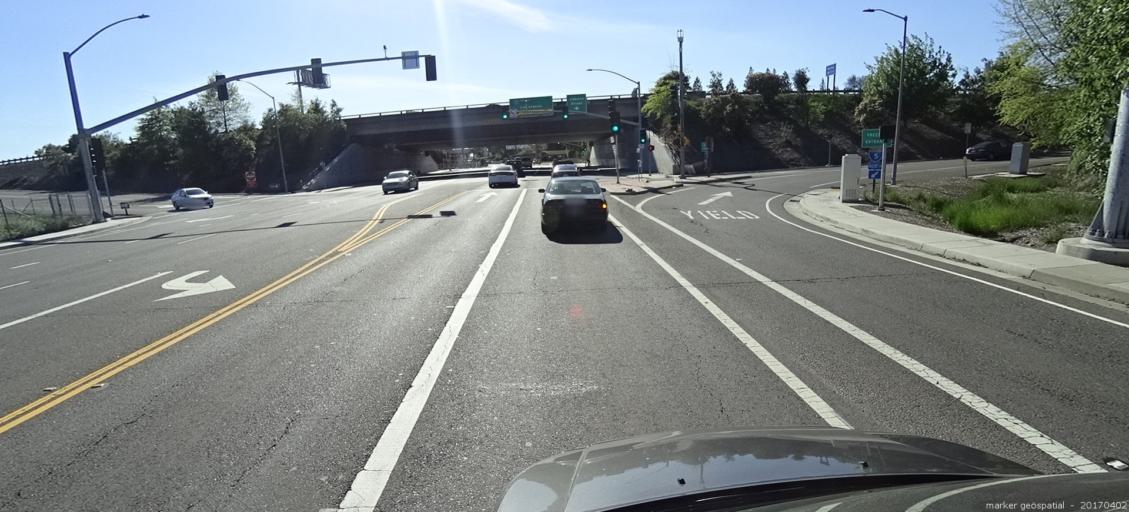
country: US
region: California
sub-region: Sacramento County
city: Sacramento
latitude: 38.5972
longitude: -121.5029
